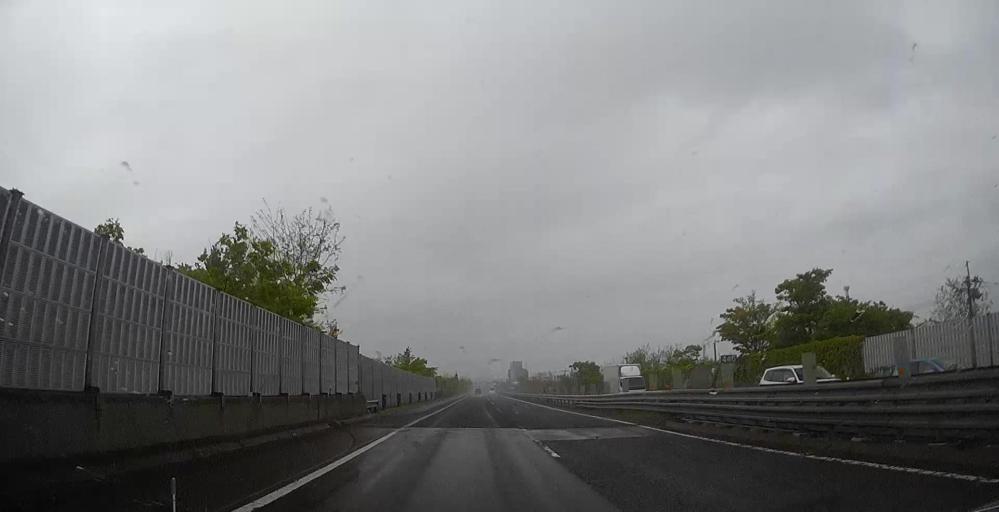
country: JP
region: Niigata
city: Tsubame
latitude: 37.6411
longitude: 138.9319
